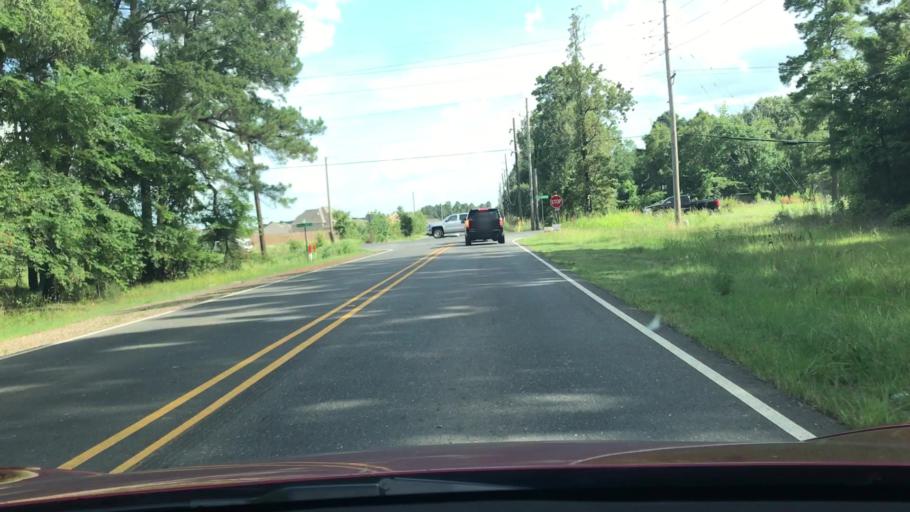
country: US
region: Louisiana
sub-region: Bossier Parish
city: Bossier City
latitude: 32.3915
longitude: -93.7385
